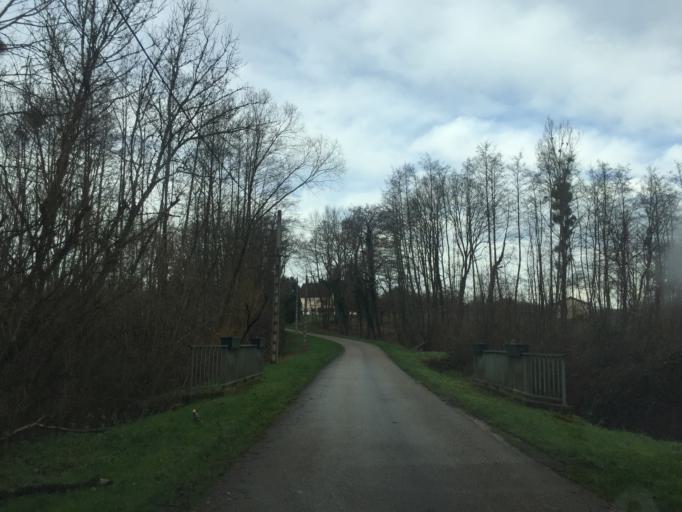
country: FR
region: Franche-Comte
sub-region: Departement du Jura
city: Chaussin
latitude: 46.9157
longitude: 5.4727
